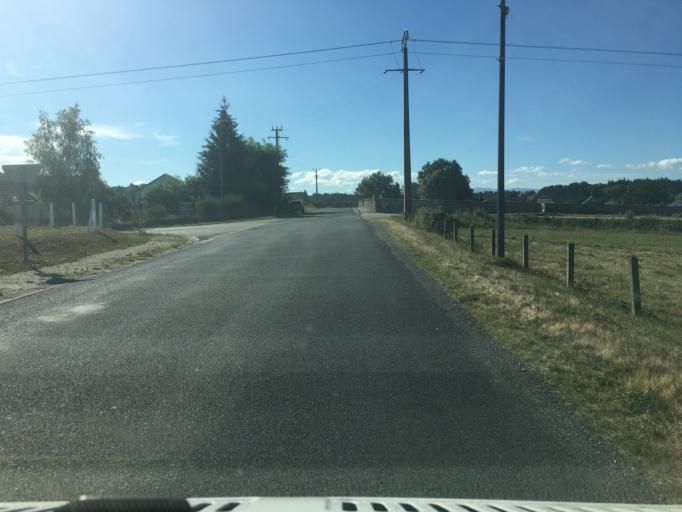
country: FR
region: Auvergne
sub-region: Departement du Cantal
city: Lanobre
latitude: 45.4384
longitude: 2.5283
